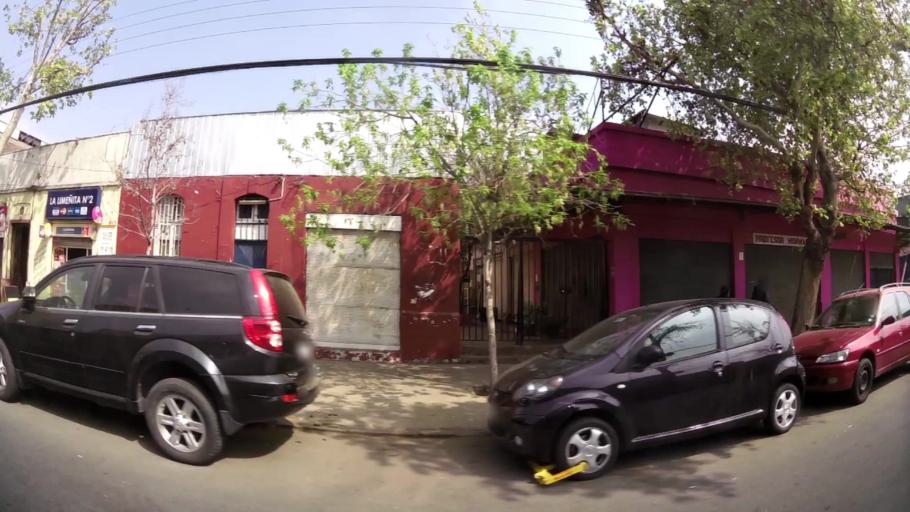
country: CL
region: Santiago Metropolitan
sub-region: Provincia de Santiago
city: Santiago
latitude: -33.4674
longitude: -70.6470
